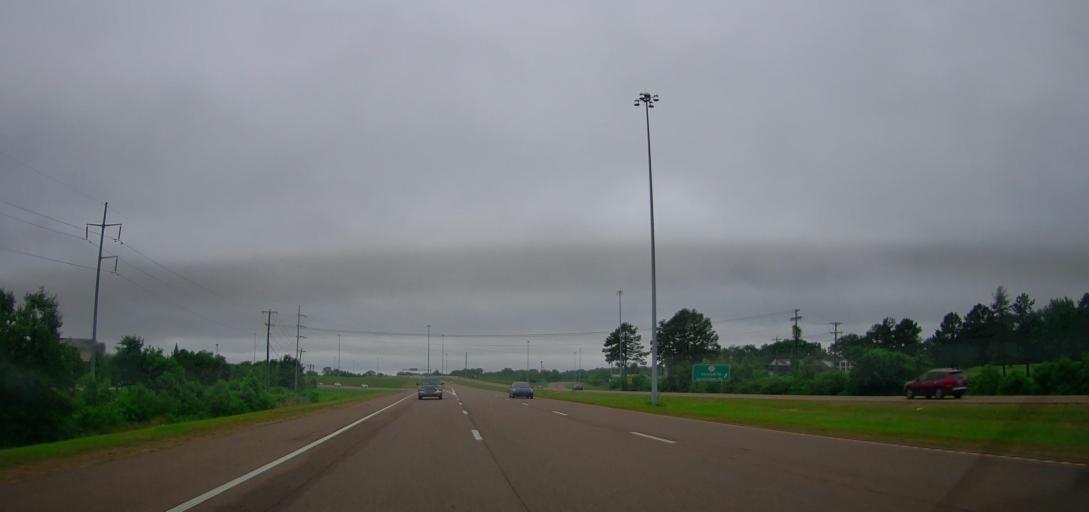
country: US
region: Mississippi
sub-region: De Soto County
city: Olive Branch
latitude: 34.9690
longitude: -89.8230
